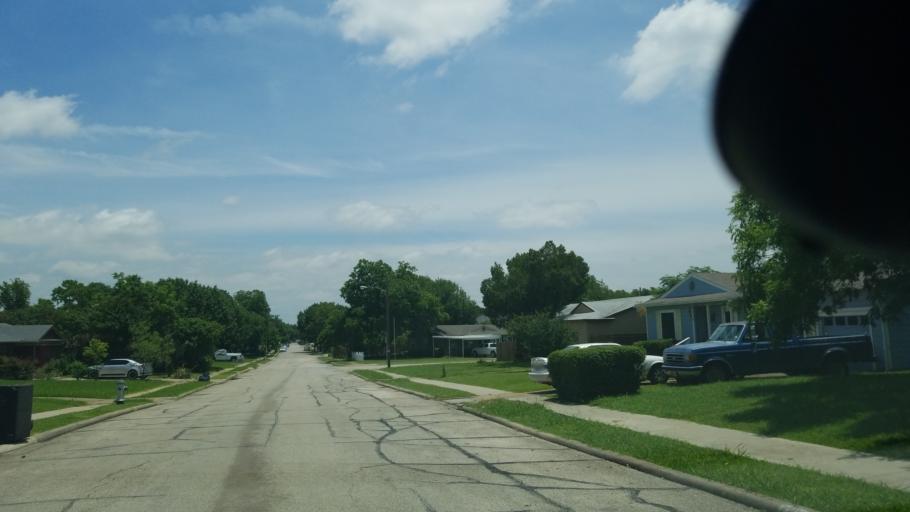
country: US
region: Texas
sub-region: Dallas County
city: Irving
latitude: 32.8464
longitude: -96.9734
